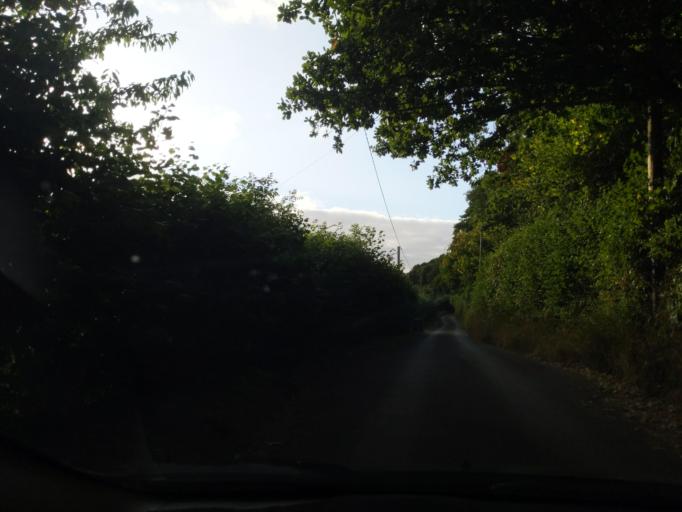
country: GB
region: England
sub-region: Devon
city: Salcombe
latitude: 50.2287
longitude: -3.7933
